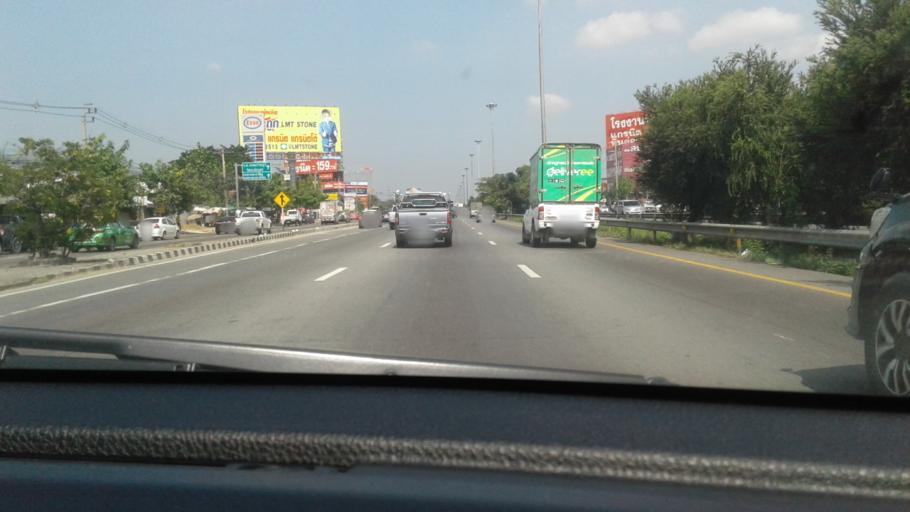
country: TH
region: Nonthaburi
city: Bang Yai
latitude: 13.8137
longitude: 100.4116
